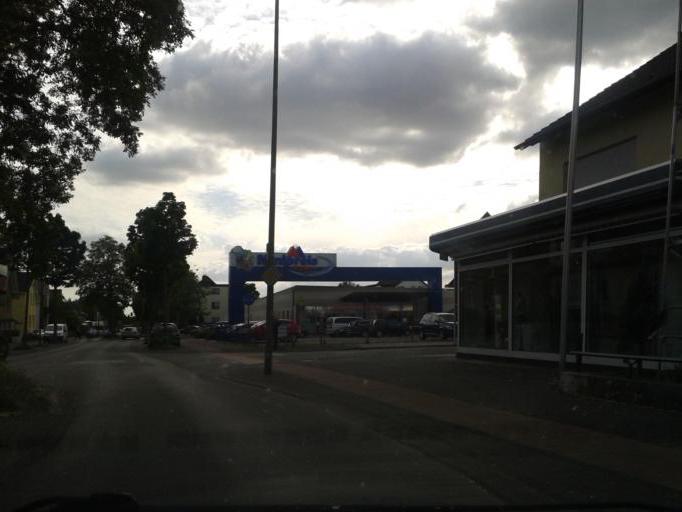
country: DE
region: North Rhine-Westphalia
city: Bad Lippspringe
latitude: 51.7789
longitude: 8.8120
